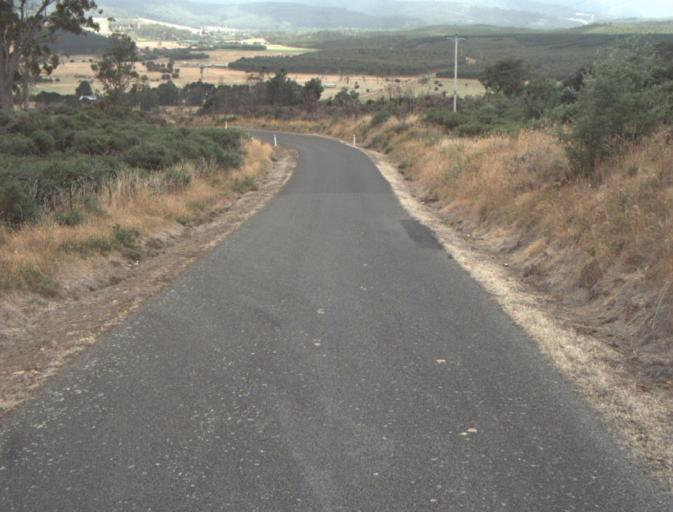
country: AU
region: Tasmania
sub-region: Northern Midlands
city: Evandale
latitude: -41.5125
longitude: 147.4739
